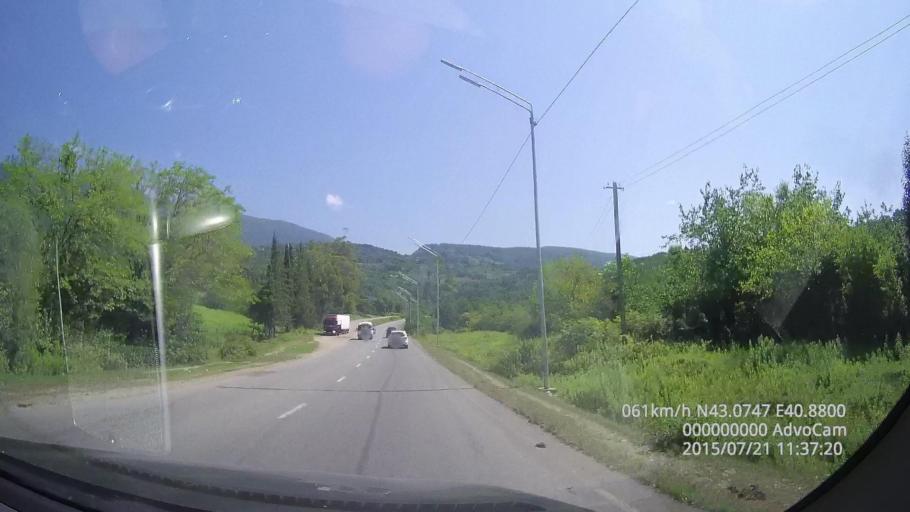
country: GE
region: Abkhazia
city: Stantsiya Novyy Afon
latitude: 43.0750
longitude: 40.8805
